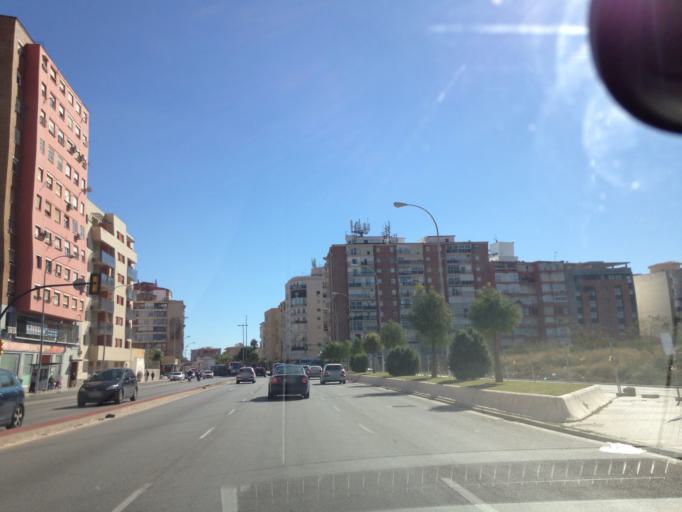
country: ES
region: Andalusia
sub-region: Provincia de Malaga
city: Malaga
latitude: 36.7052
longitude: -4.4418
